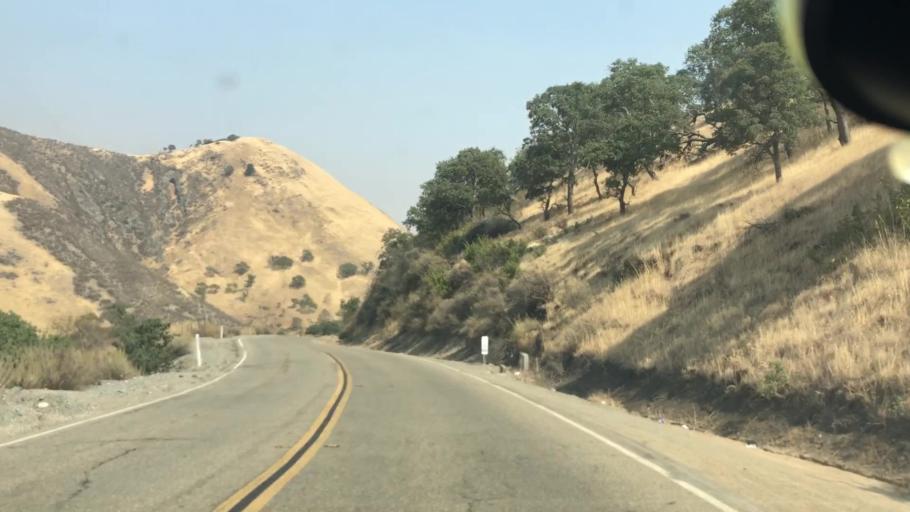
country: US
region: California
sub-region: San Joaquin County
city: Mountain House
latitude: 37.6507
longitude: -121.6025
